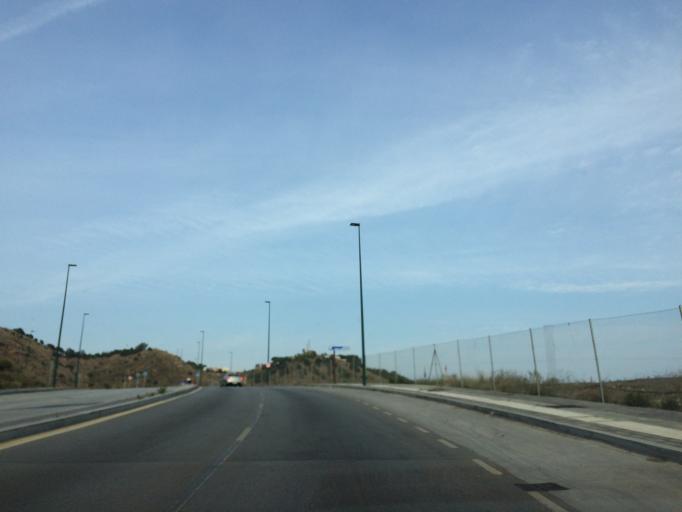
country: ES
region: Andalusia
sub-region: Provincia de Malaga
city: Malaga
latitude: 36.7365
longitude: -4.3974
